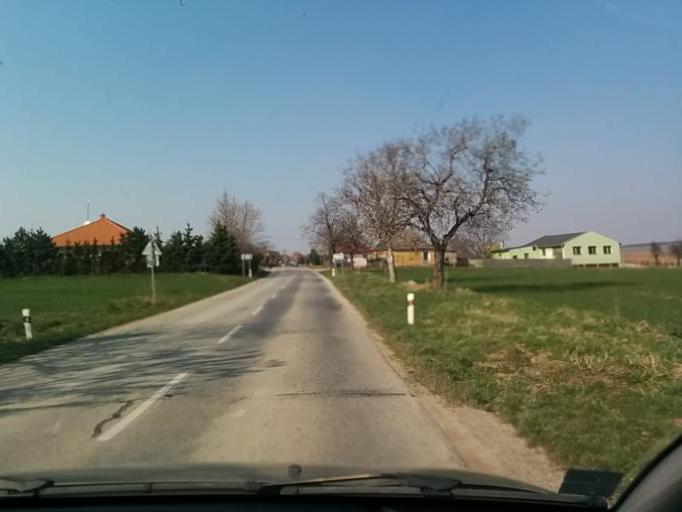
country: SK
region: Trnavsky
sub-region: Okres Galanta
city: Galanta
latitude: 48.2964
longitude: 17.7690
